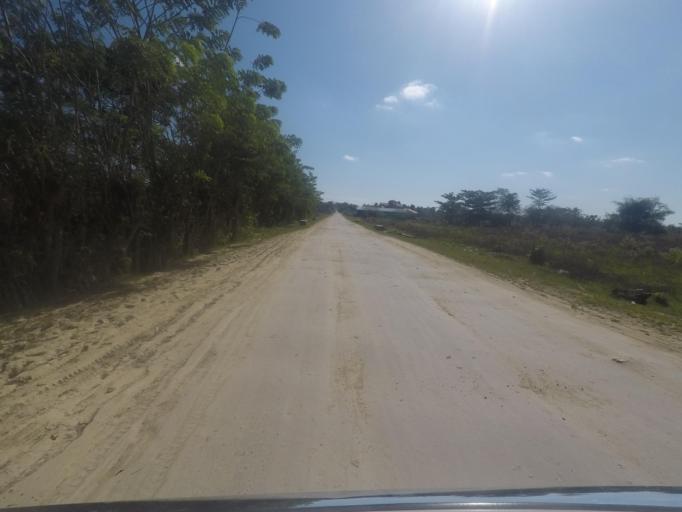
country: TL
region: Lautem
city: Lospalos
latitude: -8.5104
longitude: 127.0021
